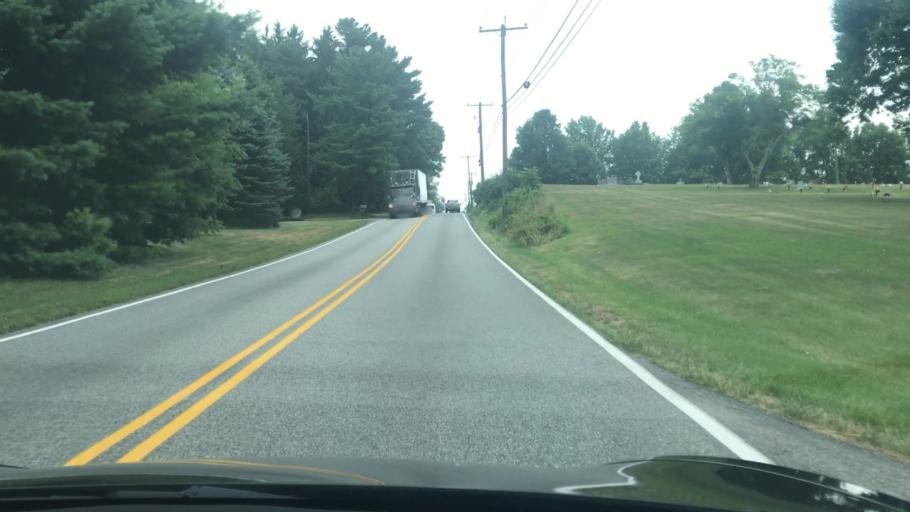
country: US
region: Pennsylvania
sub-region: York County
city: Emigsville
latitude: 40.0298
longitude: -76.7499
